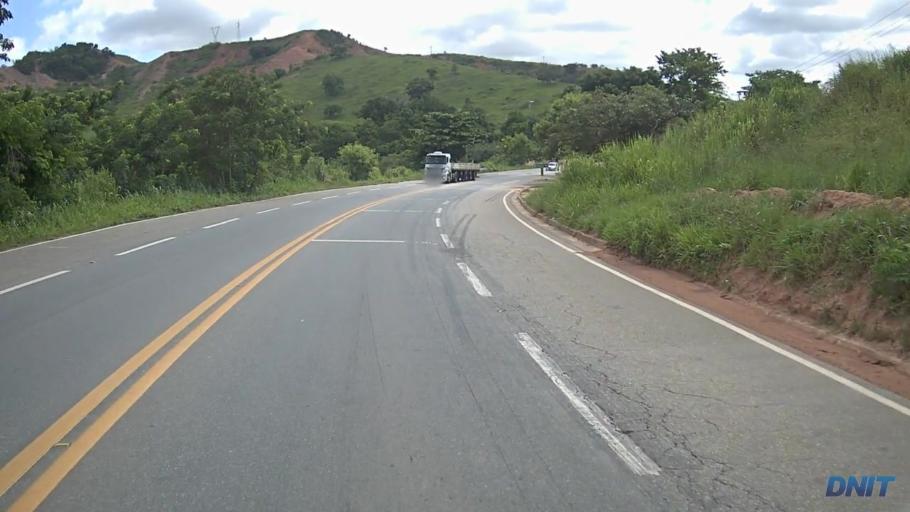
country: BR
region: Minas Gerais
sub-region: Governador Valadares
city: Governador Valadares
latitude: -18.9572
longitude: -42.0763
